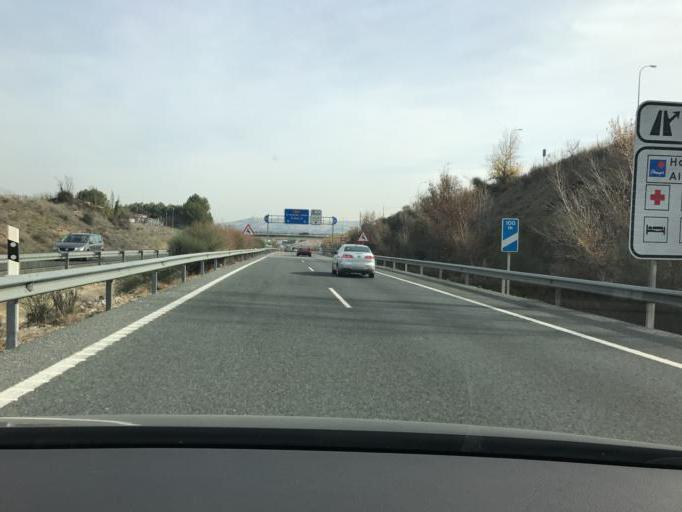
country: ES
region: Andalusia
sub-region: Provincia de Granada
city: Loja
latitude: 37.1616
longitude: -4.1262
